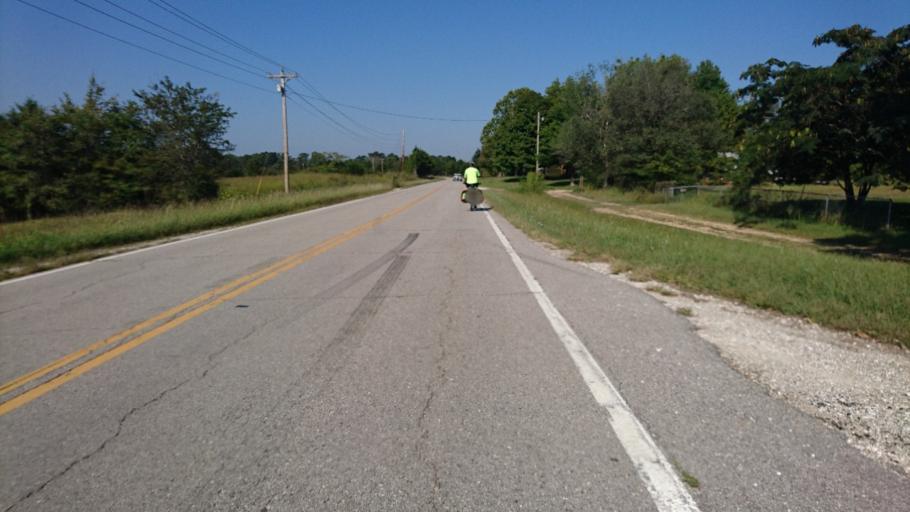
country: US
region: Missouri
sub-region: Pulaski County
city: Richland
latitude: 37.7657
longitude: -92.3839
